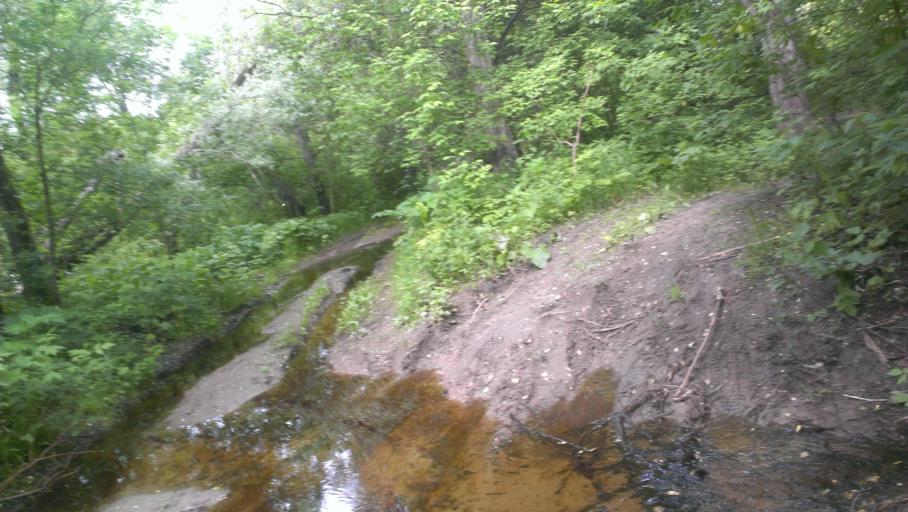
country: RU
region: Altai Krai
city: Sannikovo
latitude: 53.3421
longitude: 84.0589
